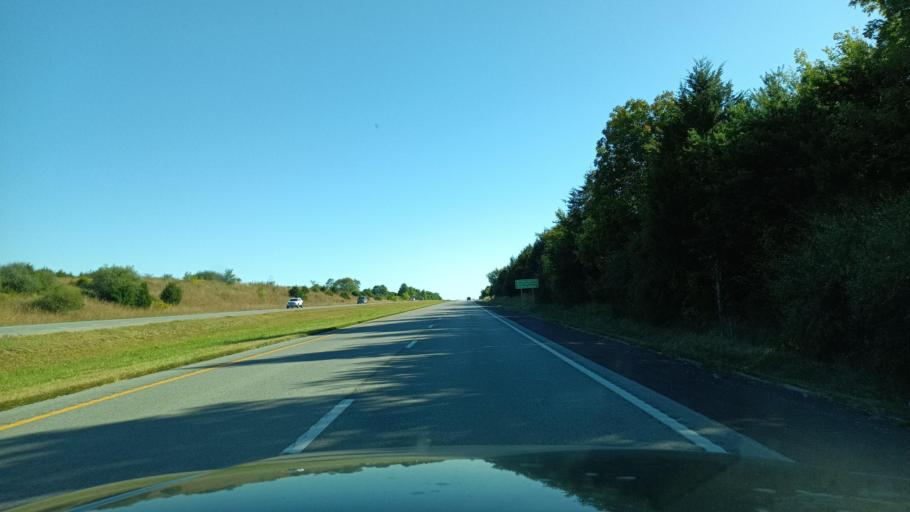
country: US
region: Missouri
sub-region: Boone County
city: Hallsville
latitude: 39.1597
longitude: -92.3310
